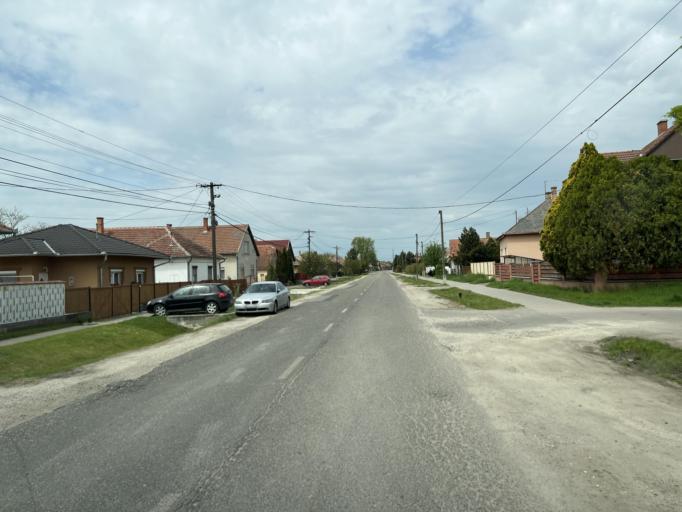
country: HU
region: Pest
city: Tortel
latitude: 47.1245
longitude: 19.9316
